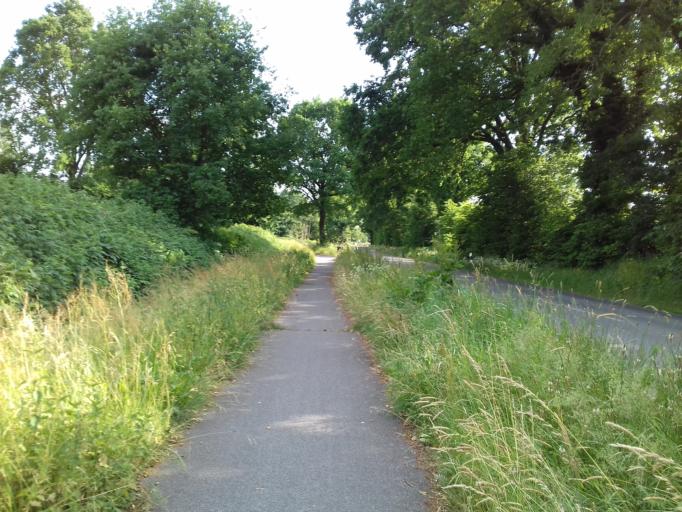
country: DE
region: Schleswig-Holstein
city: Tasdorf
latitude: 54.0817
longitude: 10.0206
